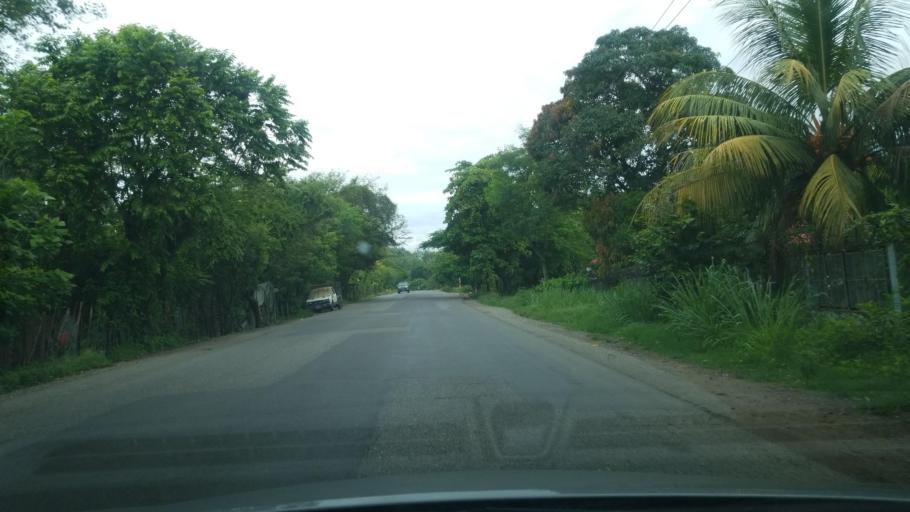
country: HN
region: Santa Barbara
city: La Flecha
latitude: 15.2998
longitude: -88.4764
